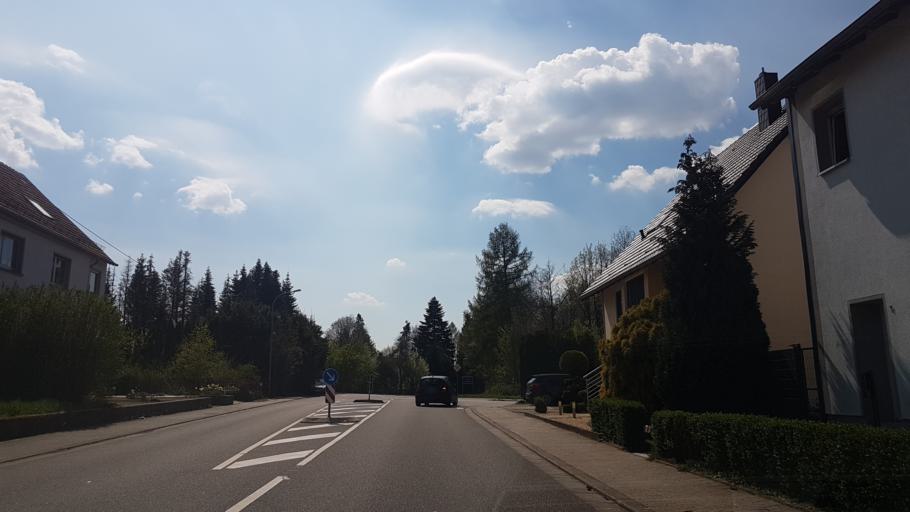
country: DE
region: Saarland
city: Quierschied
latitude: 49.3230
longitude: 6.9901
